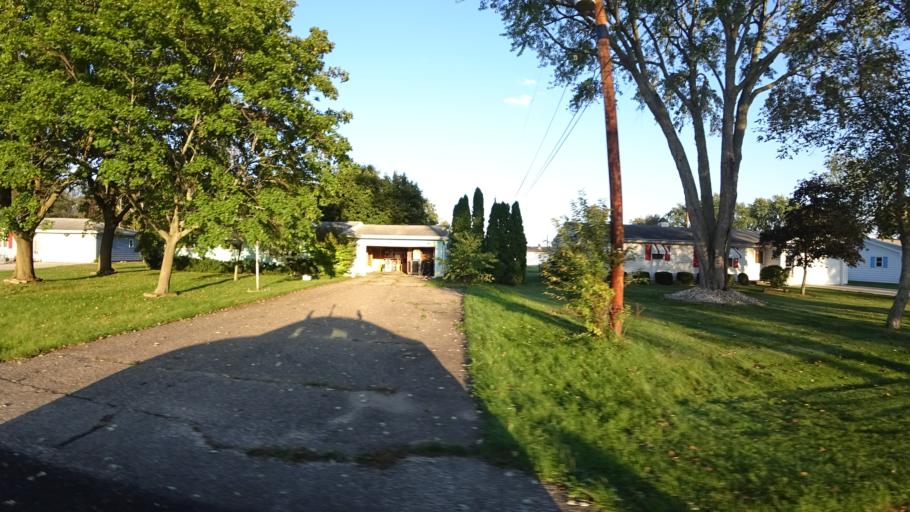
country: US
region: Michigan
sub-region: Saint Joseph County
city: Three Rivers
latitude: 41.9476
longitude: -85.6528
